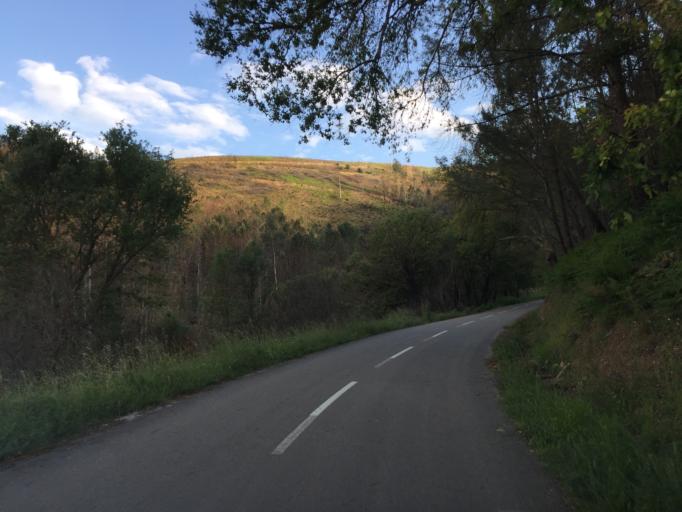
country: PT
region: Coimbra
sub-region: Arganil
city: Arganil
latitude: 40.1361
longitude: -7.9992
